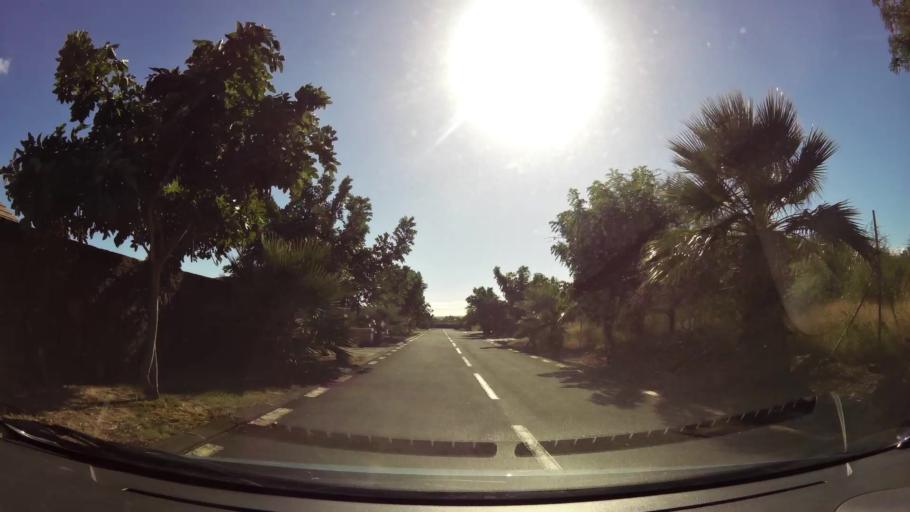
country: MU
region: Black River
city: Tamarin
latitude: -20.3374
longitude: 57.3660
